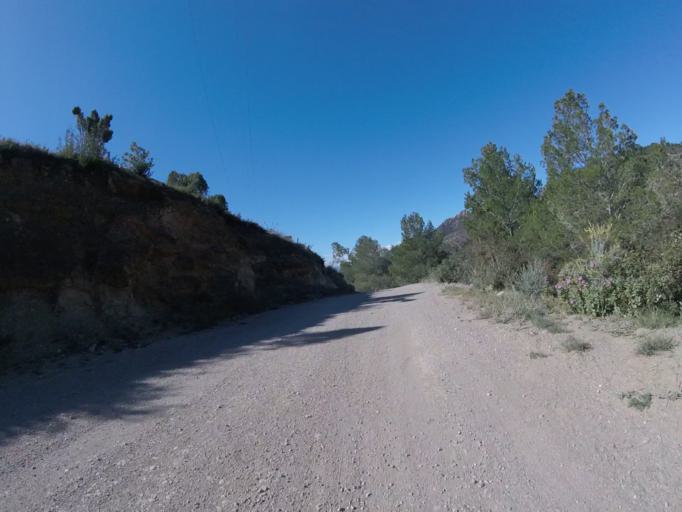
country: ES
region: Valencia
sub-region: Provincia de Castello
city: Benicassim
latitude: 40.0803
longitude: 0.0813
